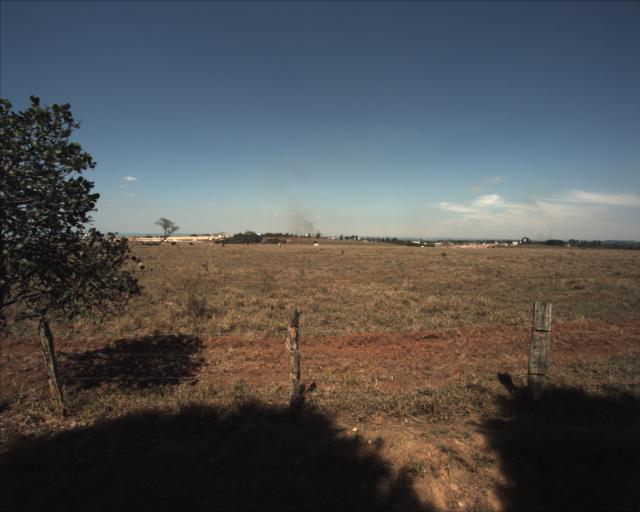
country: BR
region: Sao Paulo
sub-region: Aracoiaba Da Serra
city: Aracoiaba da Serra
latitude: -23.4858
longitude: -47.5425
